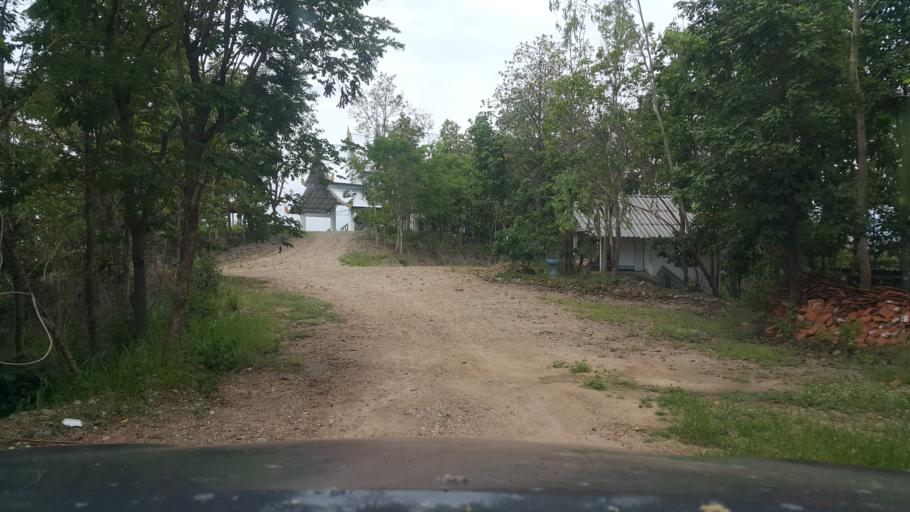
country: TH
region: Chiang Mai
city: San Pa Tong
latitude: 18.6755
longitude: 98.8330
